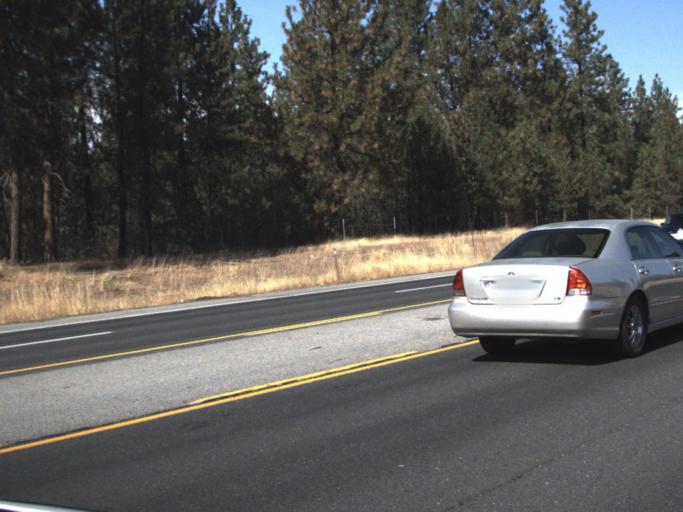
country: US
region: Washington
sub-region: Spokane County
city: Country Homes
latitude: 47.7654
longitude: -117.3867
